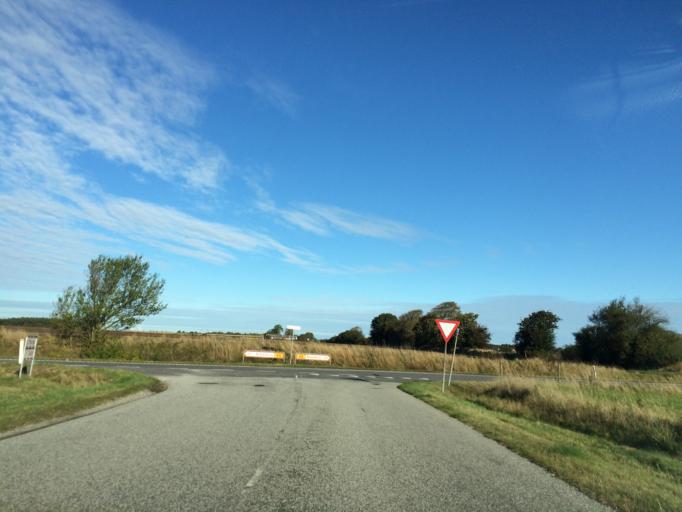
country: DK
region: Central Jutland
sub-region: Favrskov Kommune
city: Ulstrup
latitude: 56.3202
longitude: 9.7981
